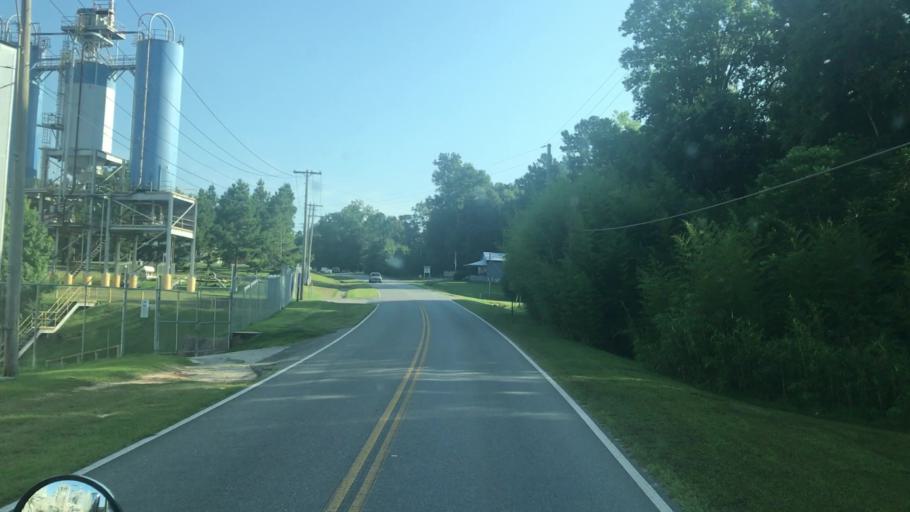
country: US
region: Florida
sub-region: Gadsden County
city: Quincy
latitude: 30.6016
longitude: -84.5724
